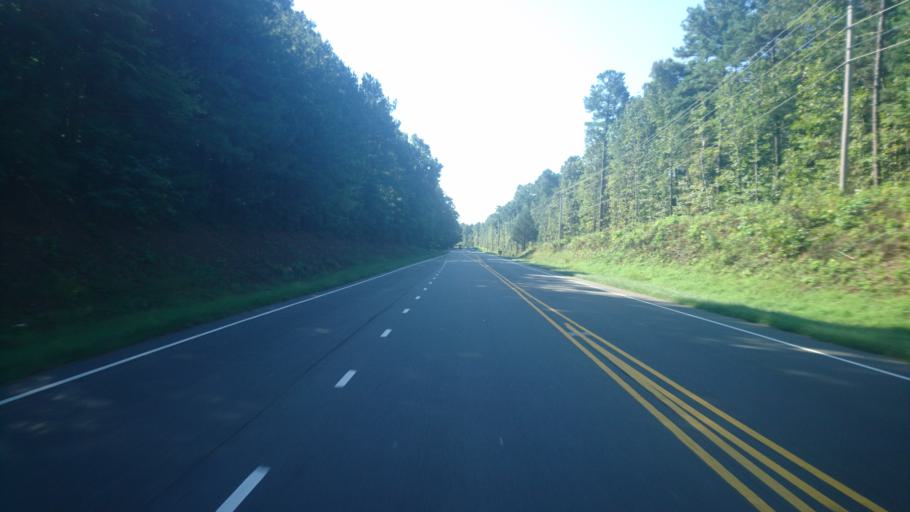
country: US
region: North Carolina
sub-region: Orange County
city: Hillsborough
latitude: 36.0266
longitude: -79.0799
